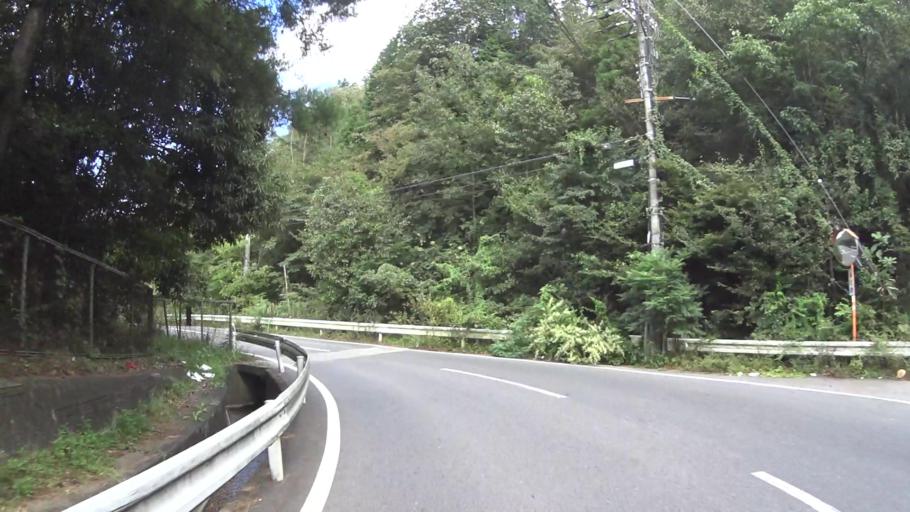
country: JP
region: Shiga Prefecture
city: Otsu-shi
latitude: 34.9330
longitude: 135.8887
